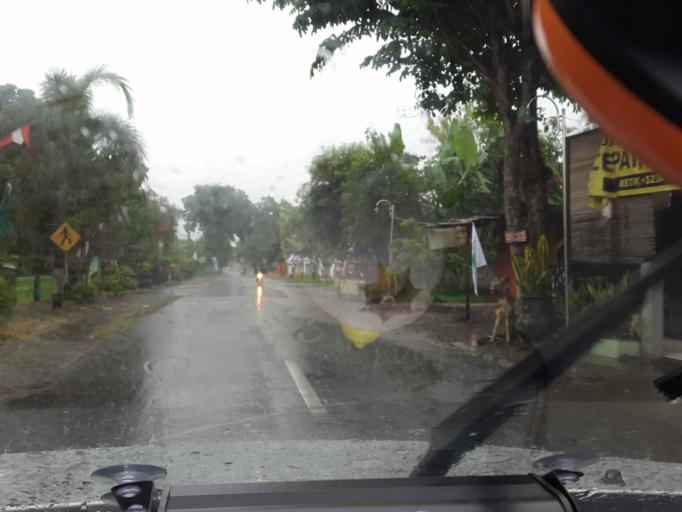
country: ID
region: Central Java
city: Jaten
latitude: -7.6044
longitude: 110.9763
